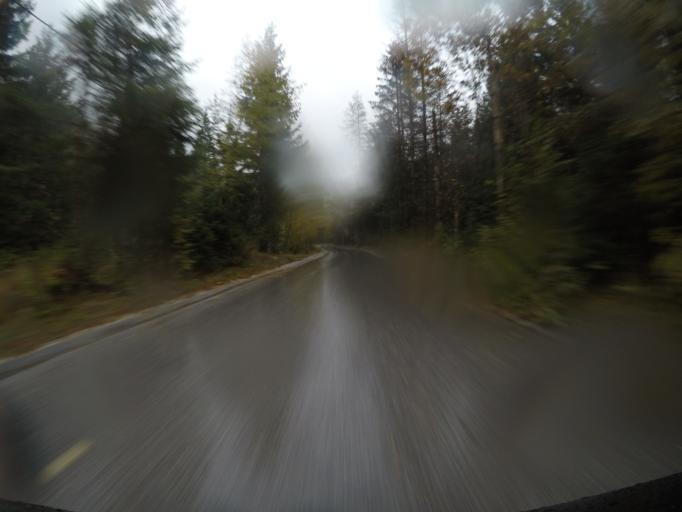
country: SI
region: Kranjska Gora
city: Kranjska Gora
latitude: 46.4078
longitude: 13.7346
